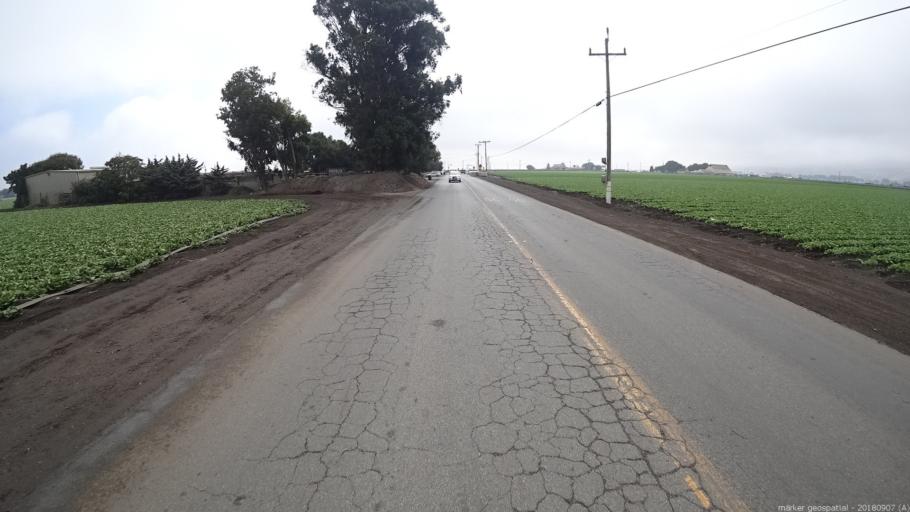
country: US
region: California
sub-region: Monterey County
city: Salinas
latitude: 36.6463
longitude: -121.6675
